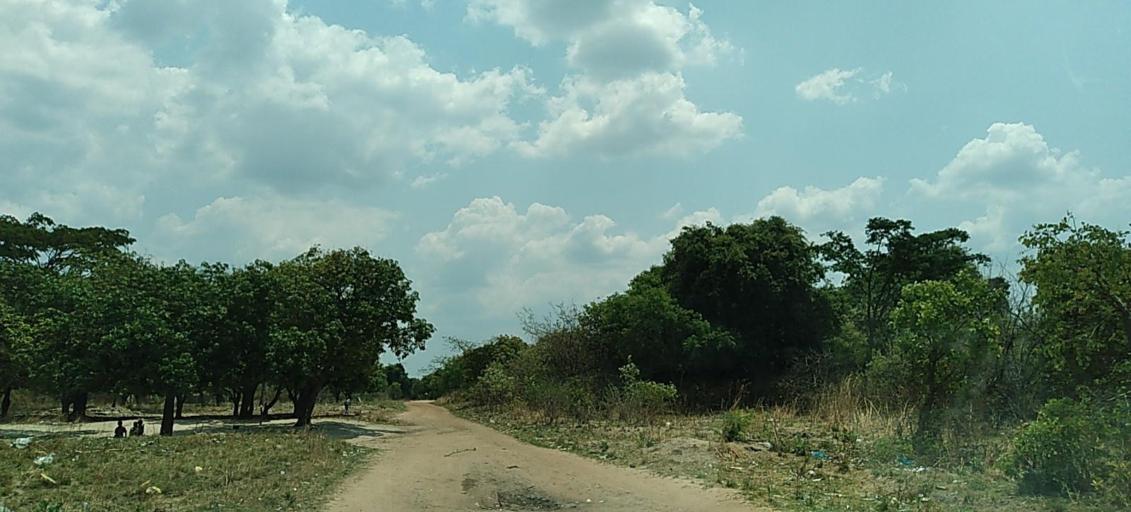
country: ZM
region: Copperbelt
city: Luanshya
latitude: -13.1567
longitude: 28.3120
